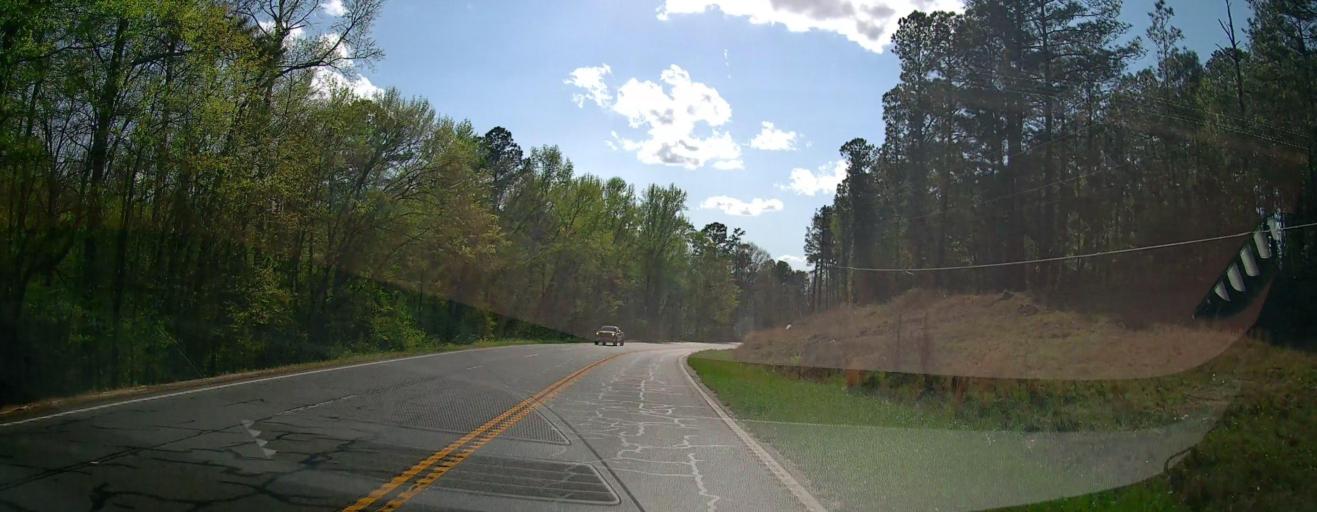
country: US
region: Georgia
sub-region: Baldwin County
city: Hardwick
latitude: 33.0903
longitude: -83.1884
